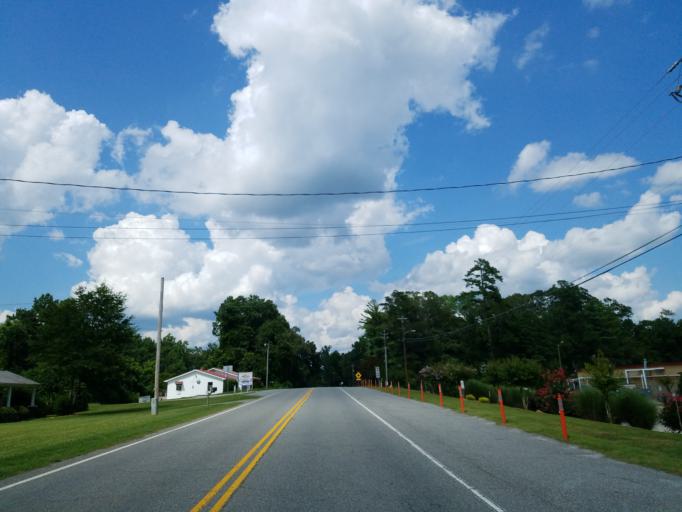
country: US
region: Georgia
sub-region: Dawson County
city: Dawsonville
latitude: 34.4238
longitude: -84.1082
